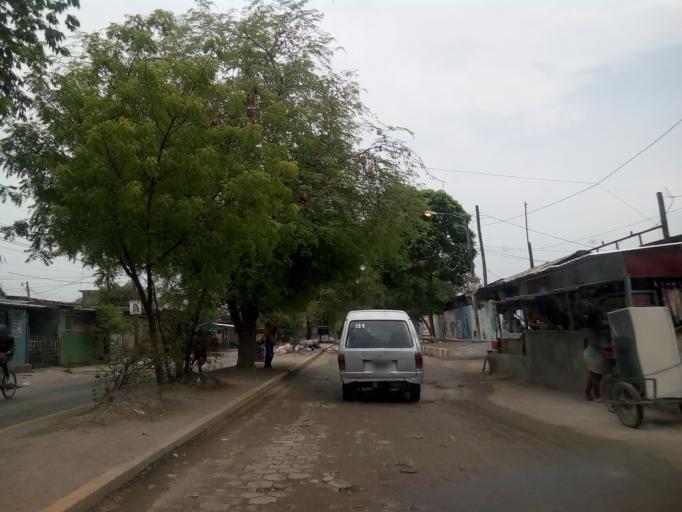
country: HN
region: Cortes
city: La Lima
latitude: 15.4597
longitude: -87.9480
